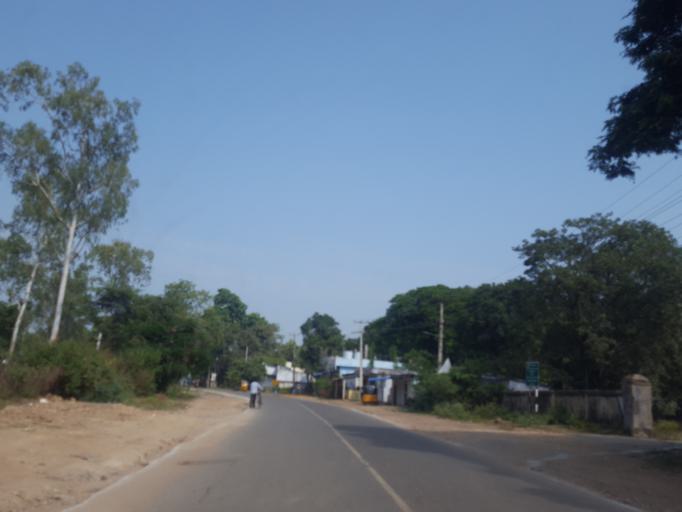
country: IN
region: Telangana
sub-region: Khammam
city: Yellandu
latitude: 17.5954
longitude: 80.3186
